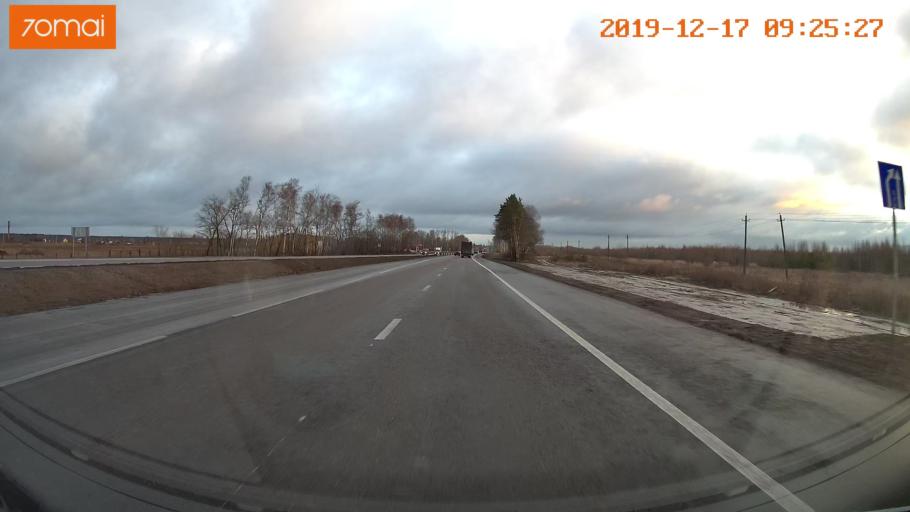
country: RU
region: Vladimir
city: Vorsha
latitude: 56.0422
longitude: 40.0557
